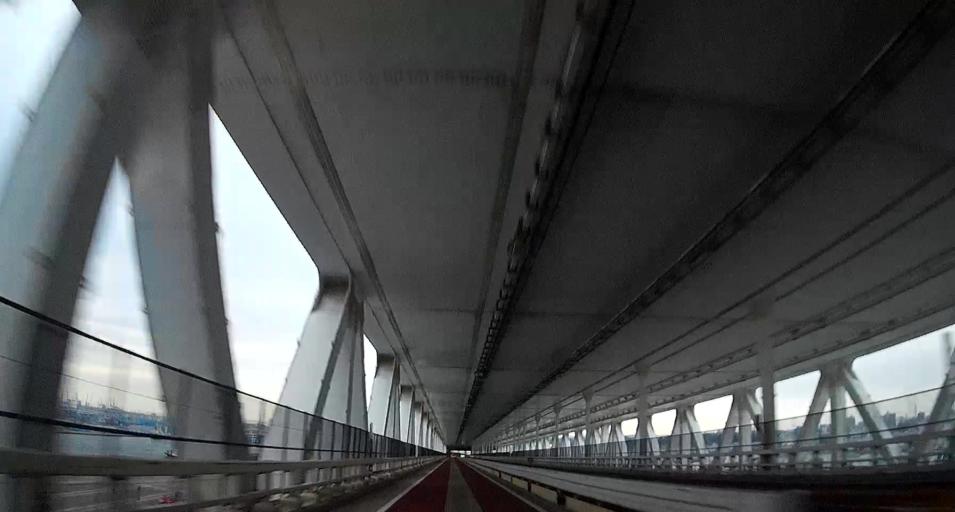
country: JP
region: Kanagawa
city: Yokohama
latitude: 35.4510
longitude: 139.6725
